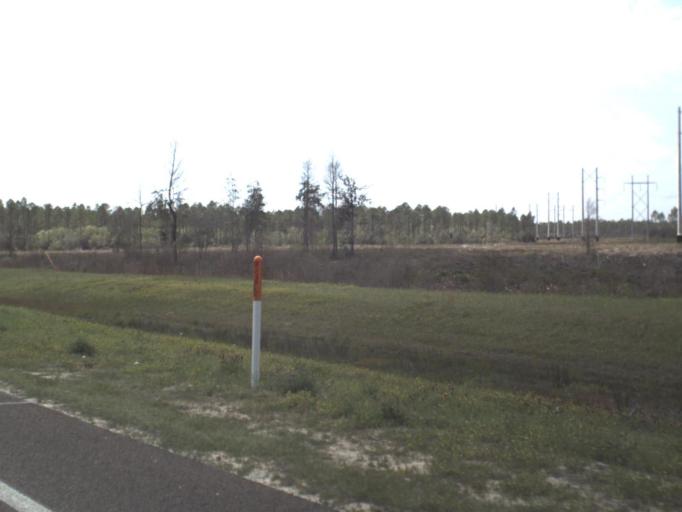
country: US
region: Florida
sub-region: Bay County
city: Laguna Beach
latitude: 30.2793
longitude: -85.8667
